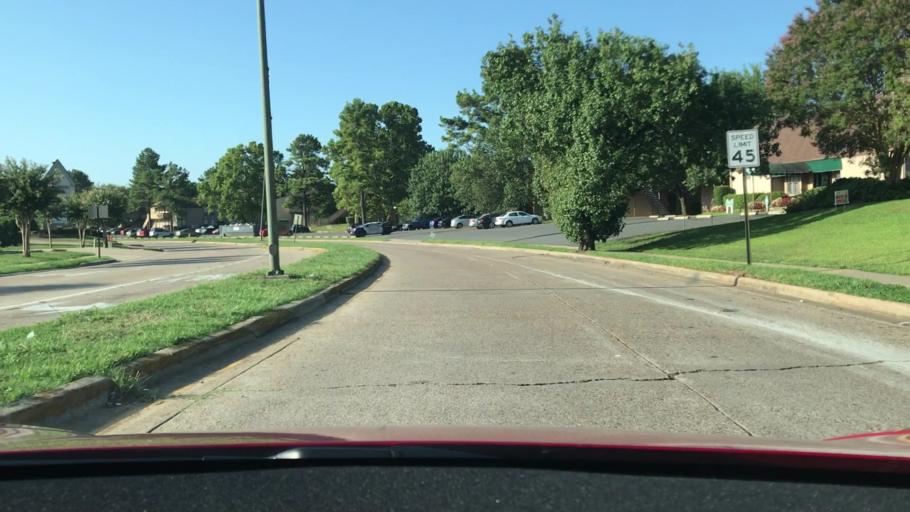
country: US
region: Louisiana
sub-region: Bossier Parish
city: Bossier City
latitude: 32.4432
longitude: -93.7298
